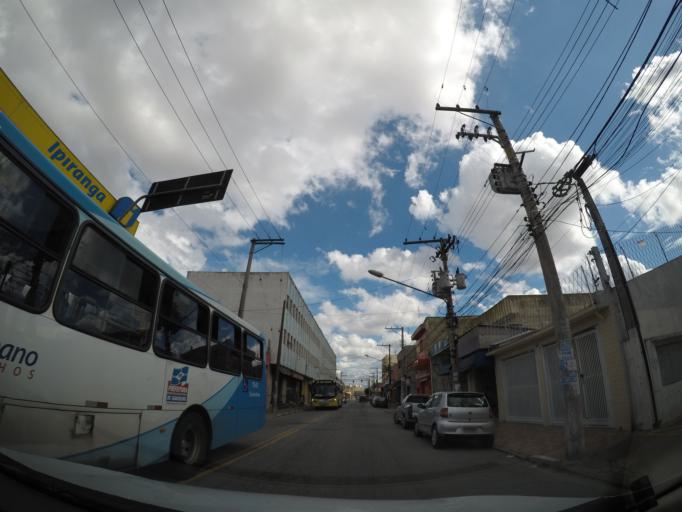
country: BR
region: Sao Paulo
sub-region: Guarulhos
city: Guarulhos
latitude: -23.4749
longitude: -46.5542
